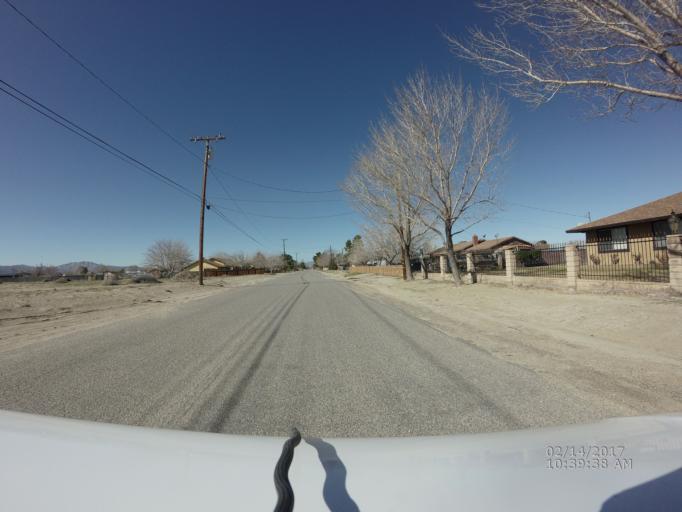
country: US
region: California
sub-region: Los Angeles County
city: Littlerock
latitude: 34.5636
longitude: -117.9349
